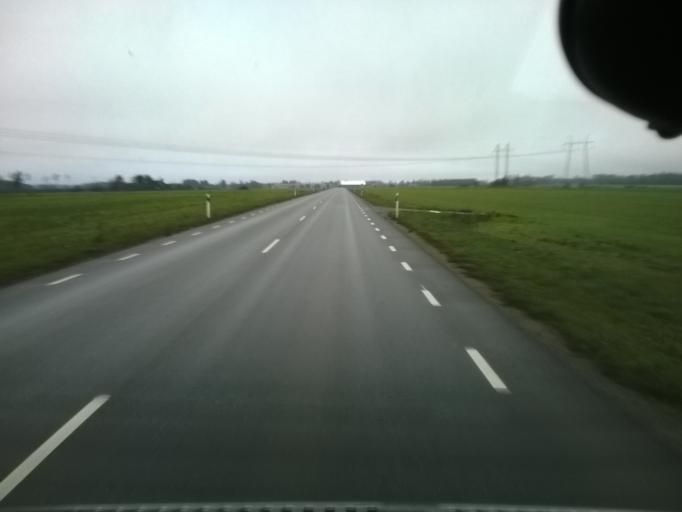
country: EE
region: Harju
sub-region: Saku vald
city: Saku
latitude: 59.2605
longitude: 24.7148
